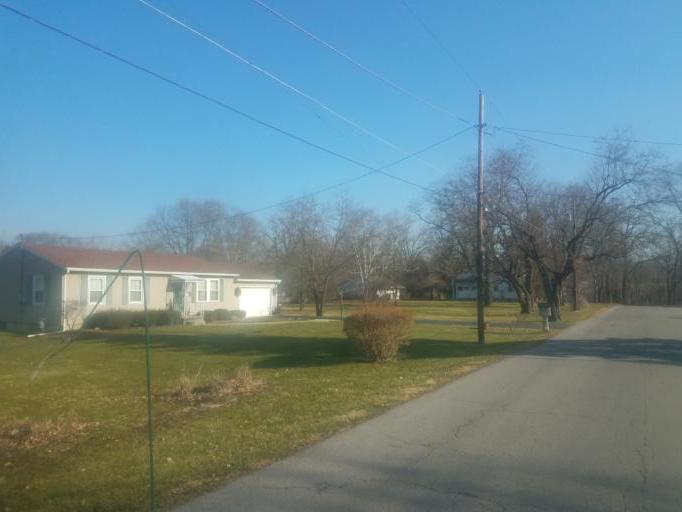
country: US
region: Ohio
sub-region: Seneca County
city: Tiffin
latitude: 41.1288
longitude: -83.1685
